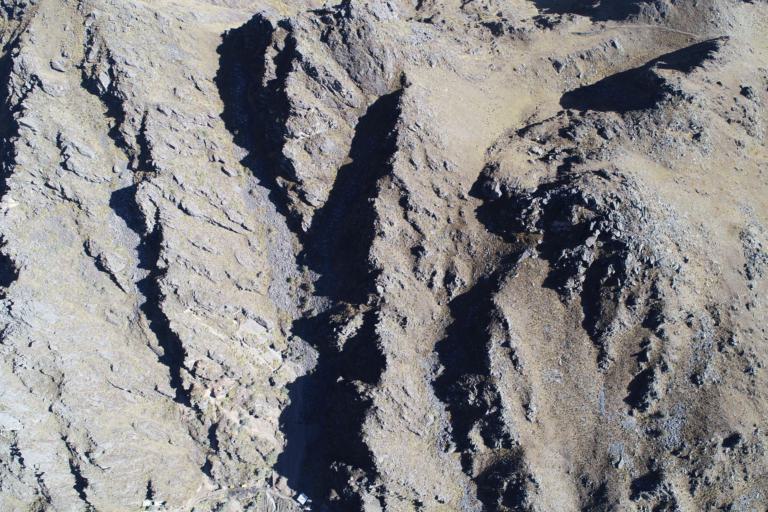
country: BO
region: La Paz
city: Sorata
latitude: -15.6549
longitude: -68.5320
